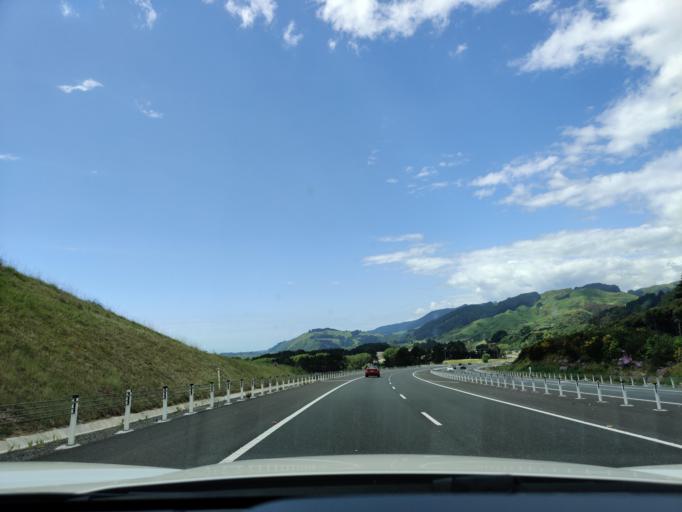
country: NZ
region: Wellington
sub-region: Kapiti Coast District
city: Paraparaumu
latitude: -40.9846
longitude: 174.9672
